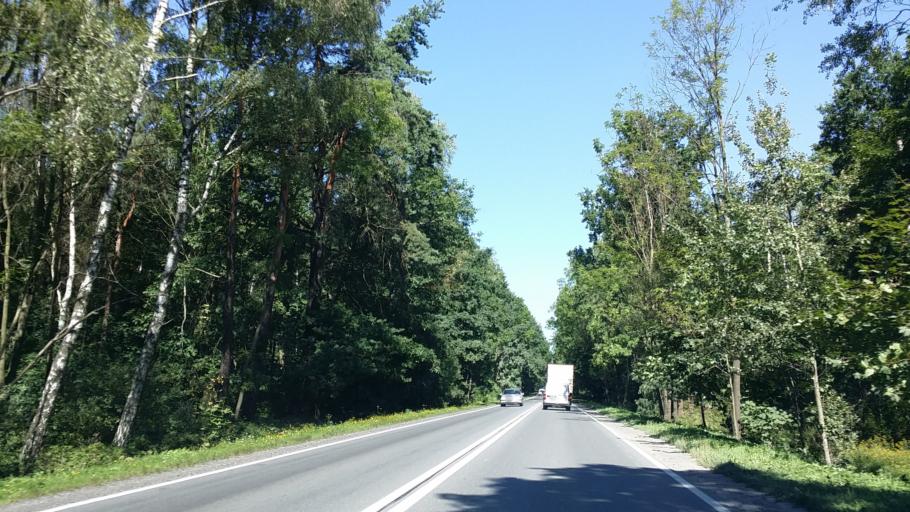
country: PL
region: Silesian Voivodeship
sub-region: Powiat bierunsko-ledzinski
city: Imielin
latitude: 50.1629
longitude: 19.1743
